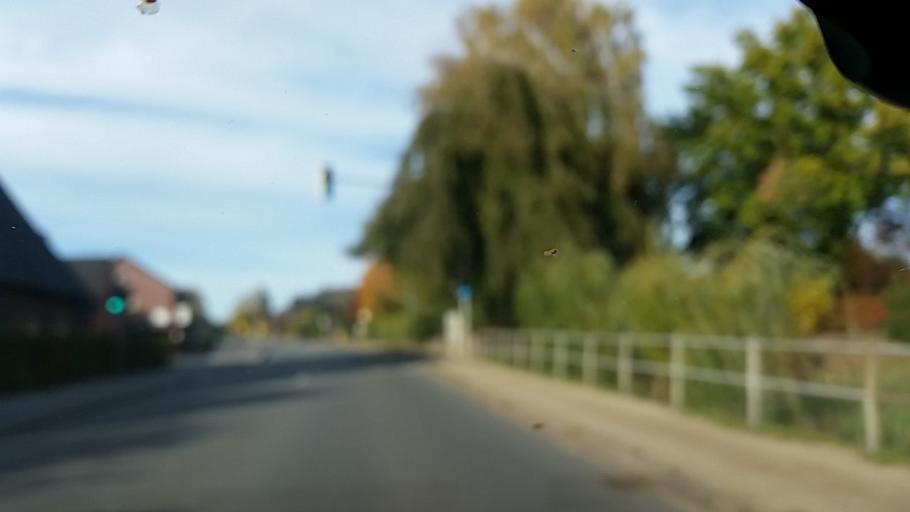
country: DE
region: Schleswig-Holstein
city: Delingsdorf
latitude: 53.7077
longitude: 10.2521
